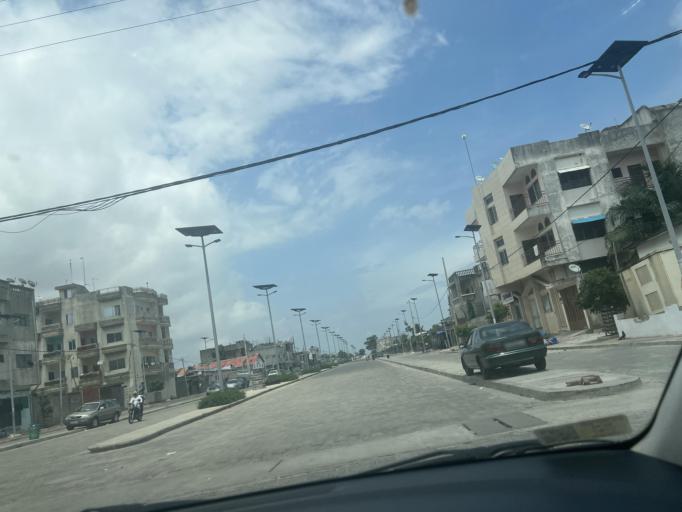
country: BJ
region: Littoral
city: Cotonou
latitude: 6.3885
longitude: 2.4470
